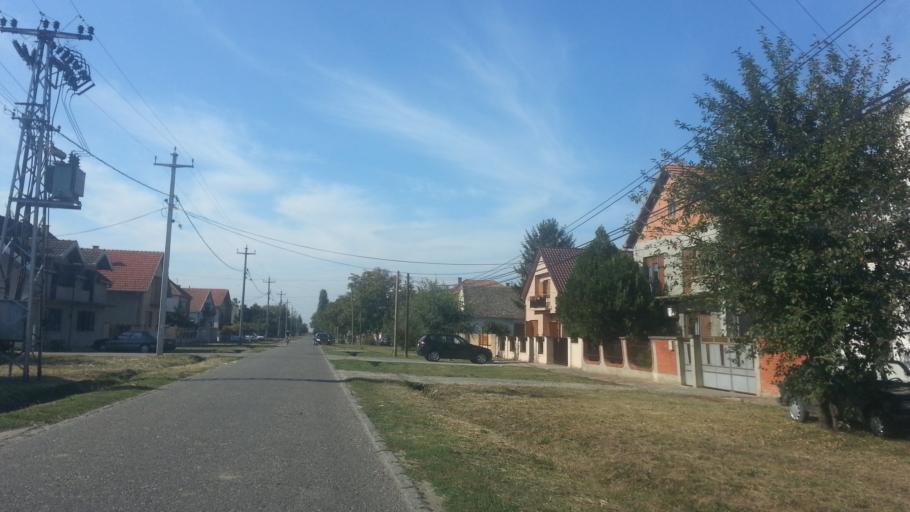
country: RS
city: Belegis
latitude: 45.0232
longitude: 20.3269
